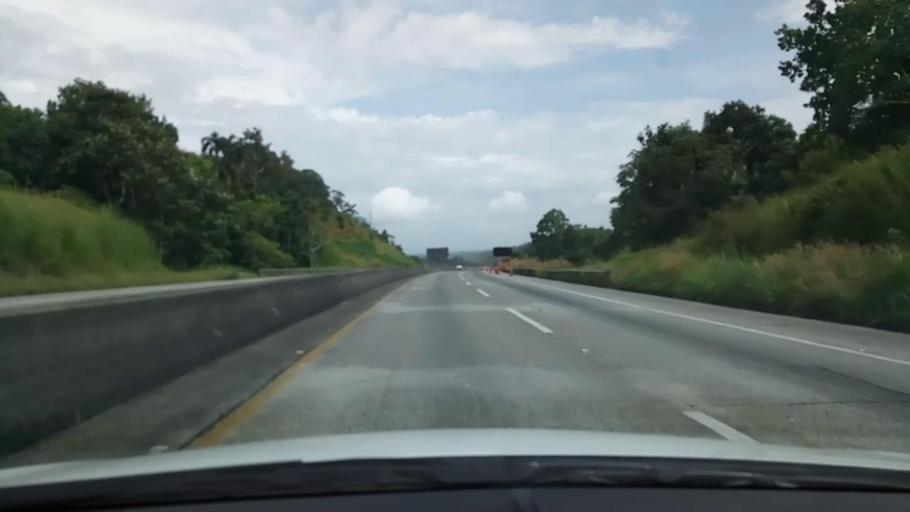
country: PA
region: Colon
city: Quebrada Bonita Adentro
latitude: 9.2832
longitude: -79.7344
